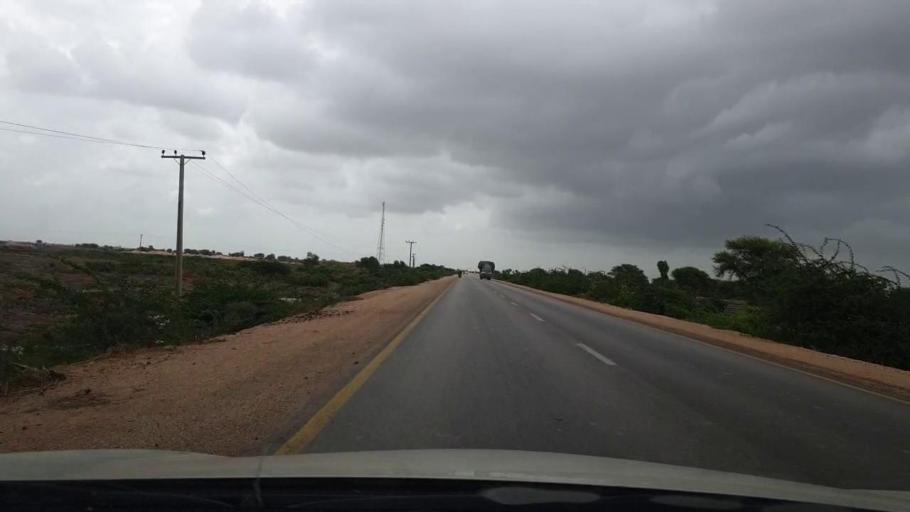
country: PK
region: Sindh
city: Mirpur Batoro
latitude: 24.6440
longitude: 68.4263
